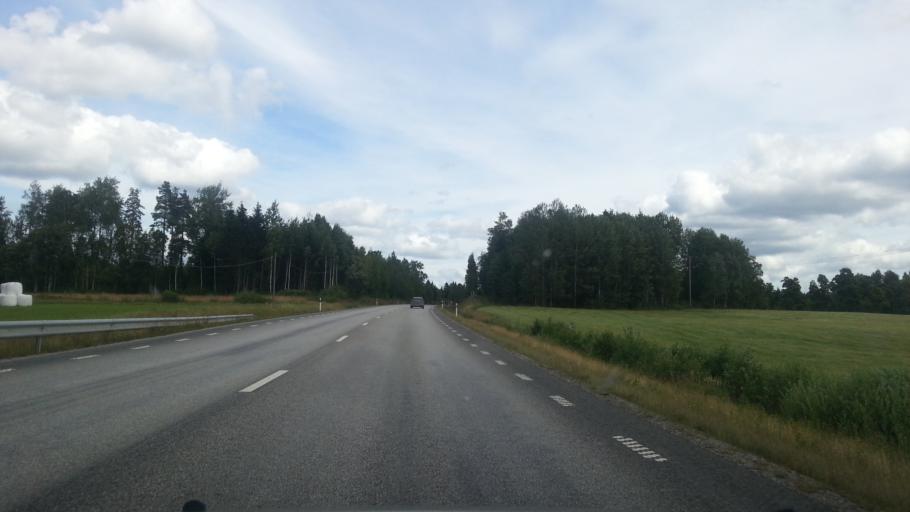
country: SE
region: OErebro
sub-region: Lindesbergs Kommun
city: Lindesberg
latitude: 59.6623
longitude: 15.2593
